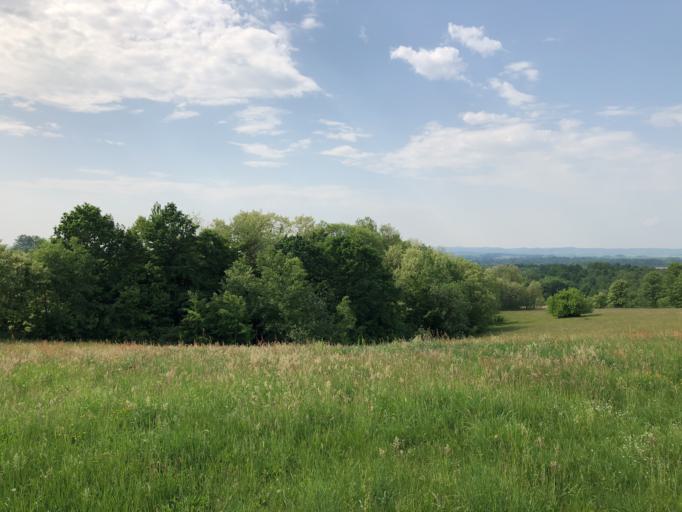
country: BA
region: Republika Srpska
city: Bosanska Gradiska
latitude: 45.0634
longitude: 17.1676
